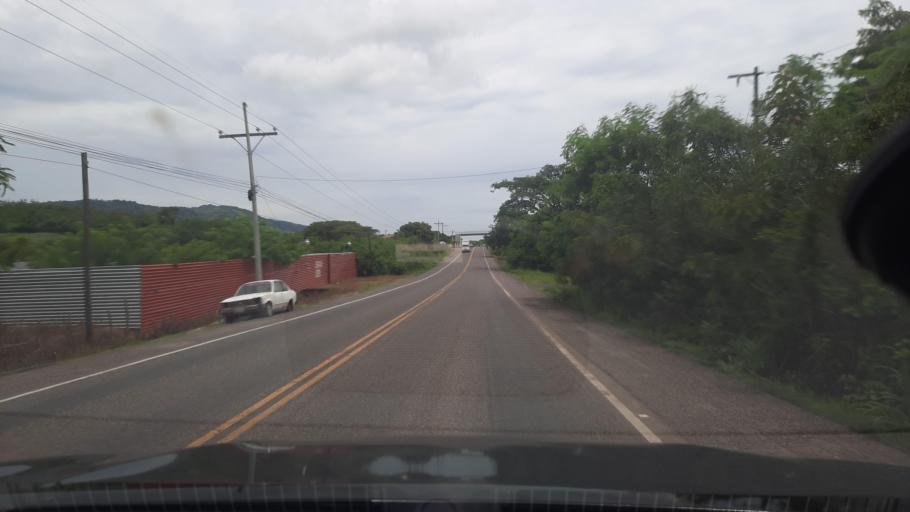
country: HN
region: Valle
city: Jicaro Galan
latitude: 13.5035
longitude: -87.4419
